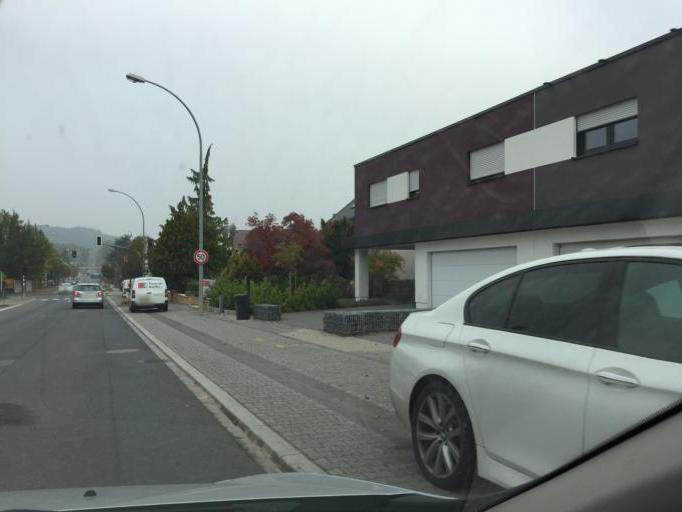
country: LU
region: Luxembourg
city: Moutfort
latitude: 49.5868
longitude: 6.2601
